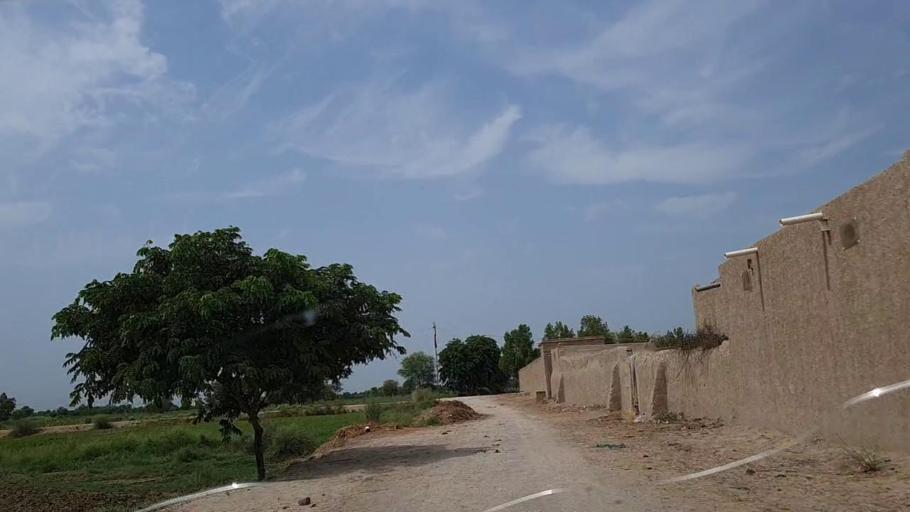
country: PK
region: Sindh
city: Tharu Shah
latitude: 26.9037
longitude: 68.0749
